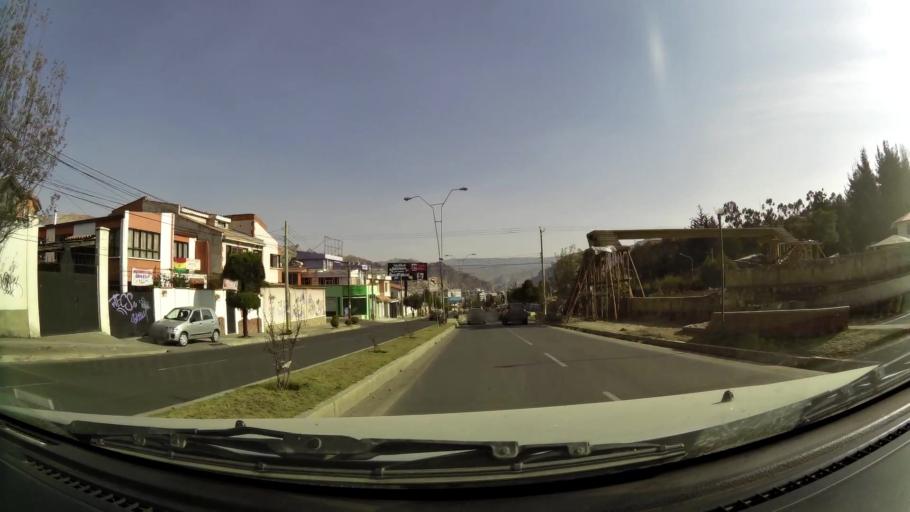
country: BO
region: La Paz
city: La Paz
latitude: -16.5325
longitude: -68.0762
